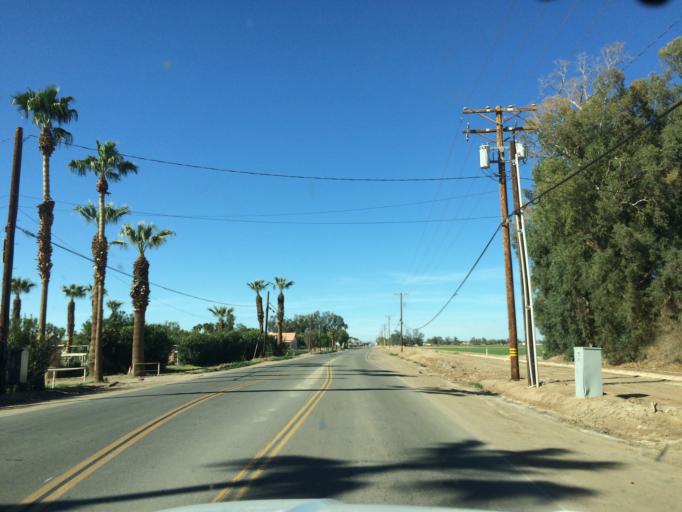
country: US
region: California
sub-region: Imperial County
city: Heber
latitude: 32.7528
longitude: -115.5605
